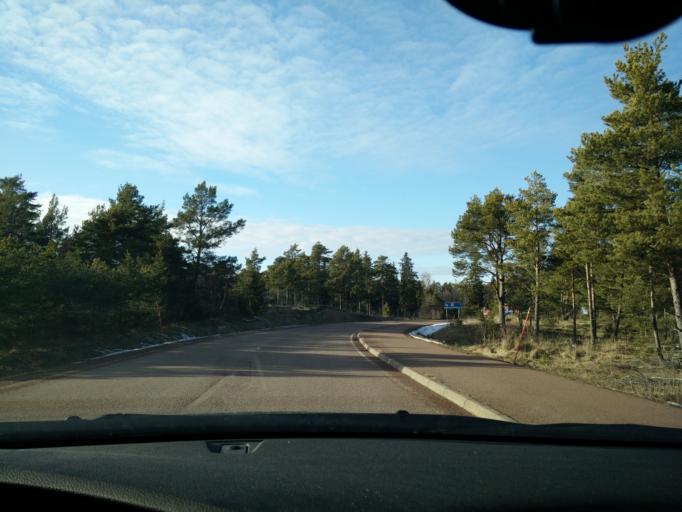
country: AX
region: Alands landsbygd
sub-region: Eckeroe
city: Eckeroe
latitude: 60.2293
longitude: 19.5471
